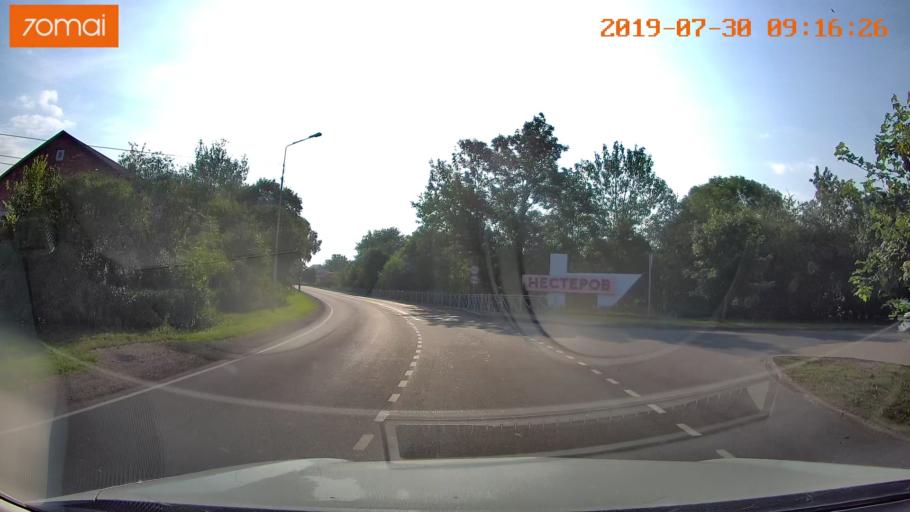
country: RU
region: Kaliningrad
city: Nesterov
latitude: 54.6336
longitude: 22.5580
